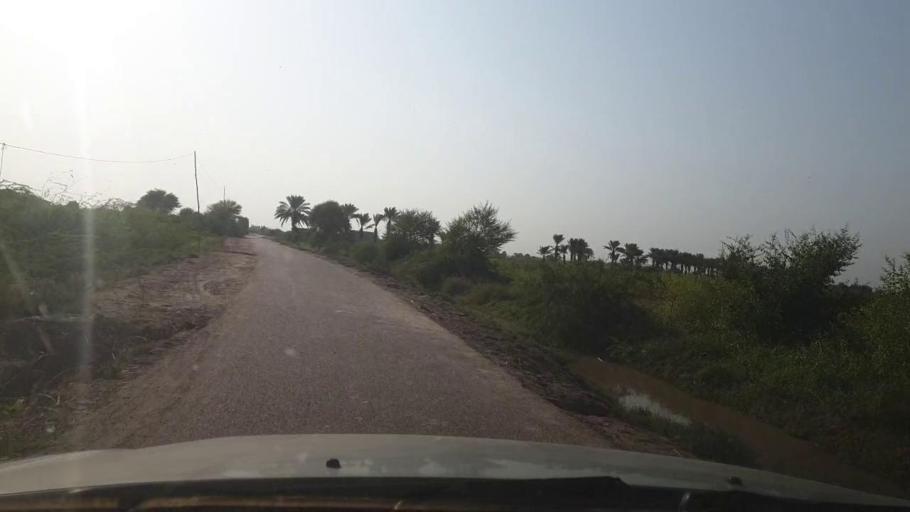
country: PK
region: Sindh
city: Tando Ghulam Ali
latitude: 25.1834
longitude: 68.9487
